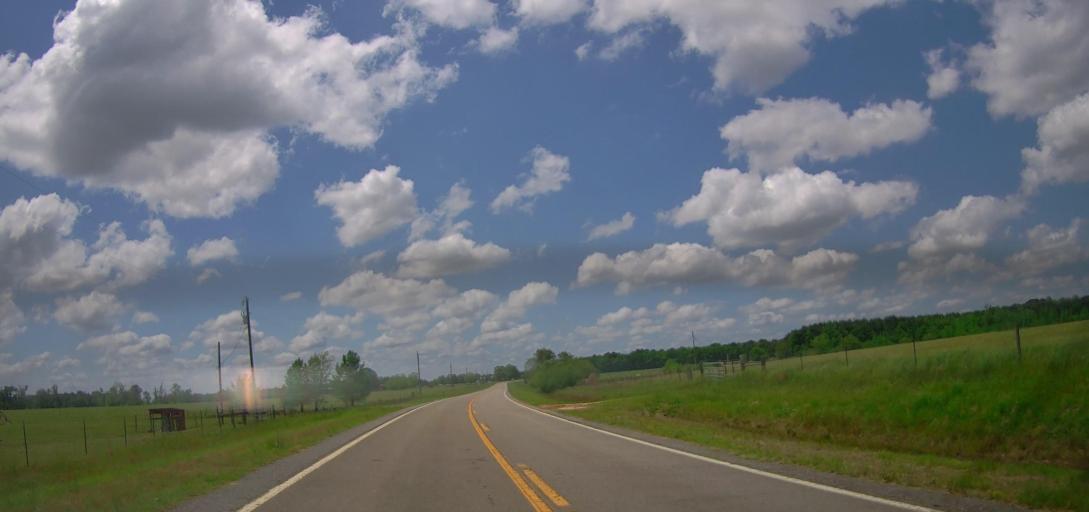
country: US
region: Georgia
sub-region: Dodge County
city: Chester
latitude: 32.5458
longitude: -83.1797
